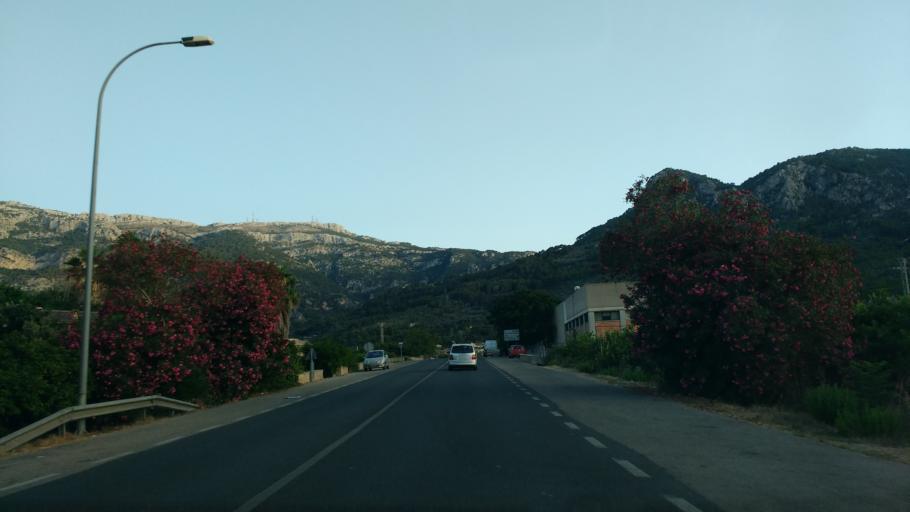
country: ES
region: Balearic Islands
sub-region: Illes Balears
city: Soller
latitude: 39.7761
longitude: 2.7057
